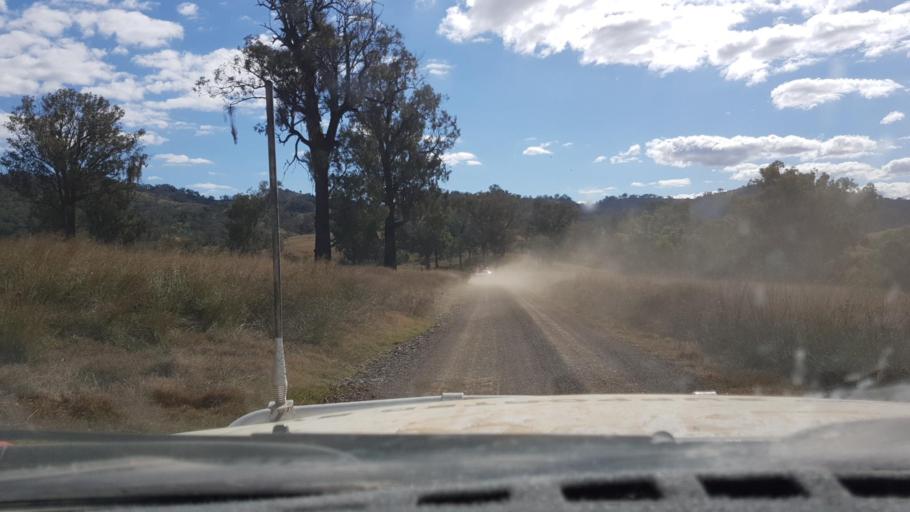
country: AU
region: New South Wales
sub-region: Tamworth Municipality
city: Manilla
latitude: -30.4507
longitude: 150.7803
